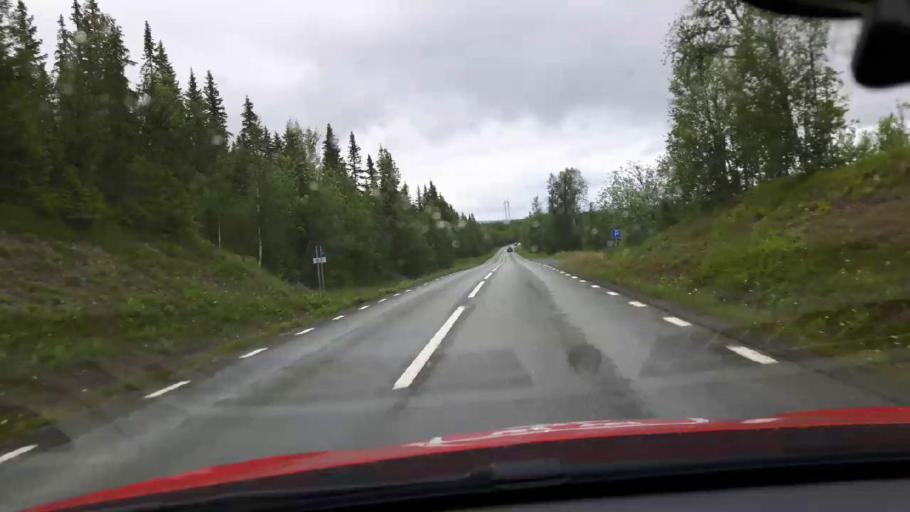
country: SE
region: Jaemtland
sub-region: Are Kommun
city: Are
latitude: 63.3290
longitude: 12.5574
